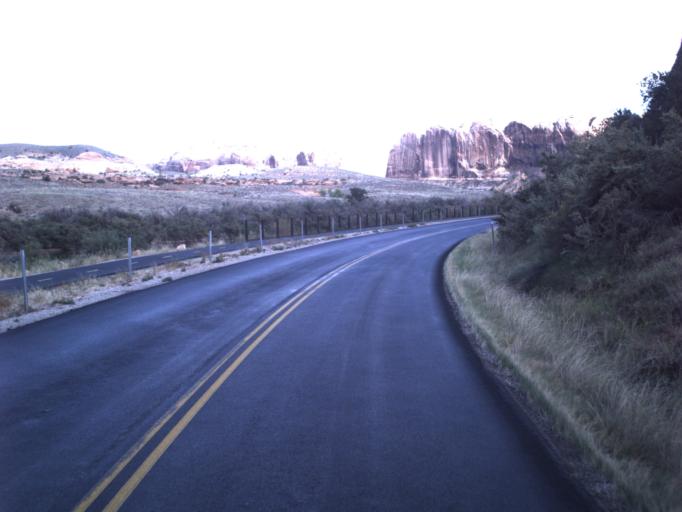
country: US
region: Utah
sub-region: Grand County
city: Moab
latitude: 38.6132
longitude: -109.5539
